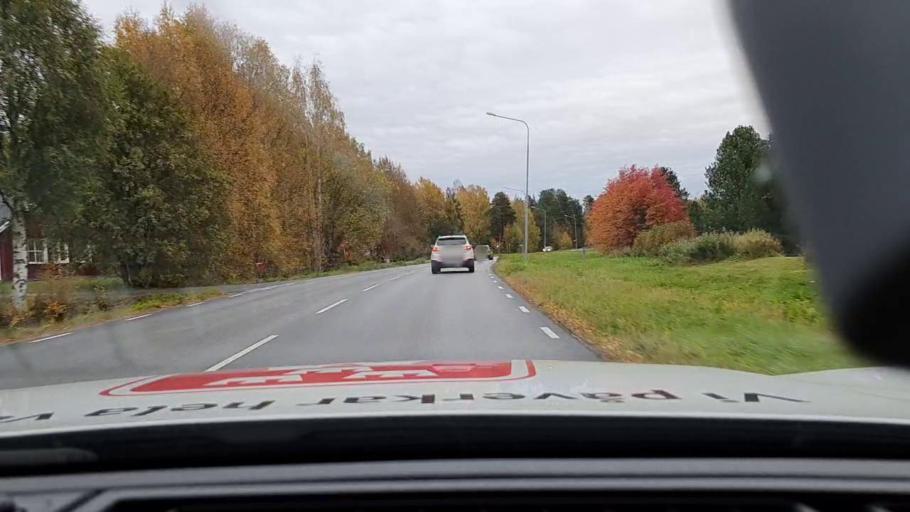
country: SE
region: Norrbotten
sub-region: Bodens Kommun
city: Saevast
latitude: 65.7700
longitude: 21.7272
